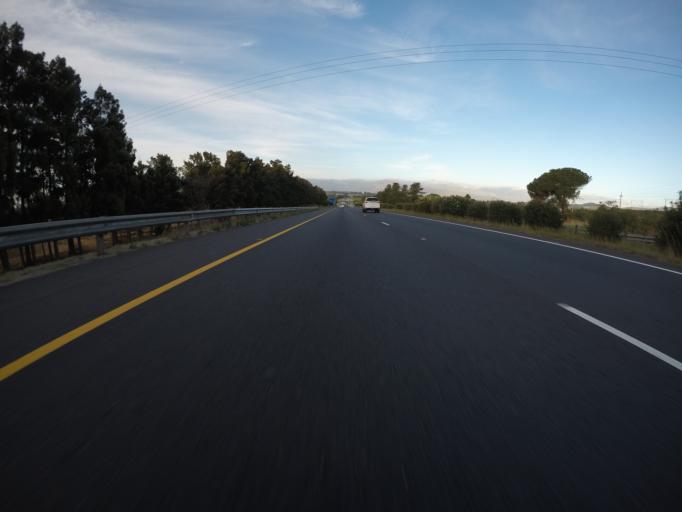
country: ZA
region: Western Cape
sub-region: Cape Winelands District Municipality
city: Stellenbosch
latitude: -33.8043
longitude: 18.8469
